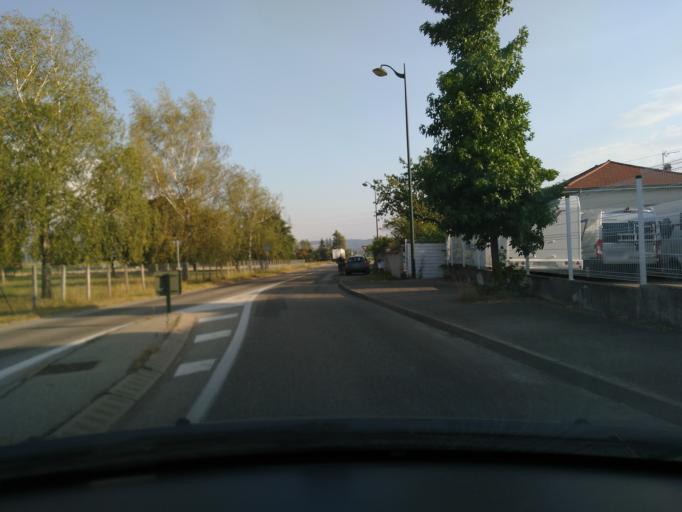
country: FR
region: Rhone-Alpes
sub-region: Departement de l'Isere
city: La Cote-Saint-Andre
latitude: 45.3815
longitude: 5.2629
